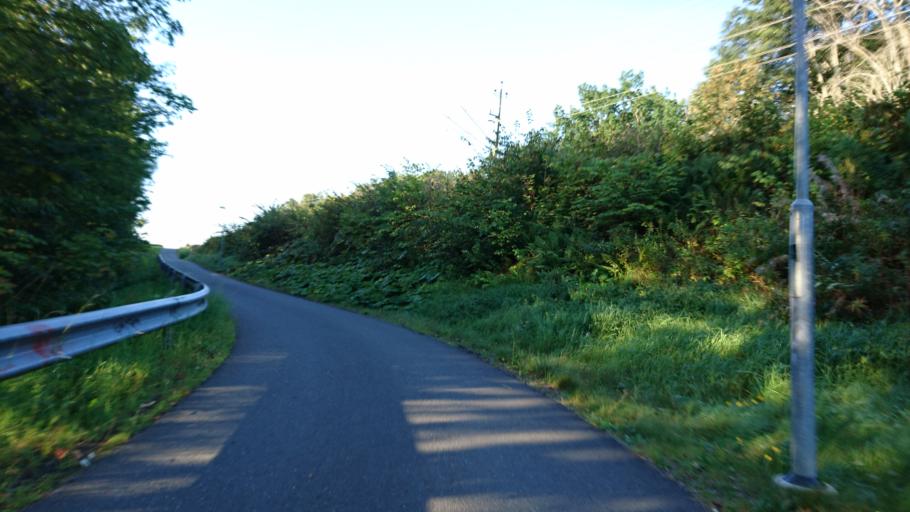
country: SE
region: Joenkoeping
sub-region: Jonkopings Kommun
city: Jonkoping
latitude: 57.8088
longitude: 14.1525
